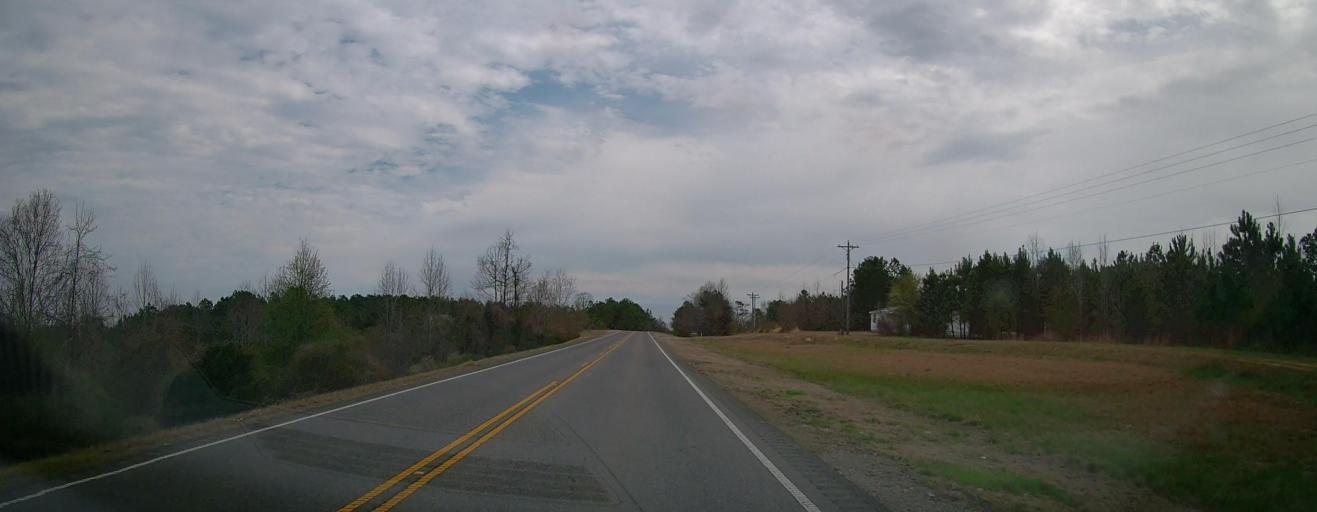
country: US
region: Alabama
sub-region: Marion County
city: Guin
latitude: 34.0310
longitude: -87.9441
